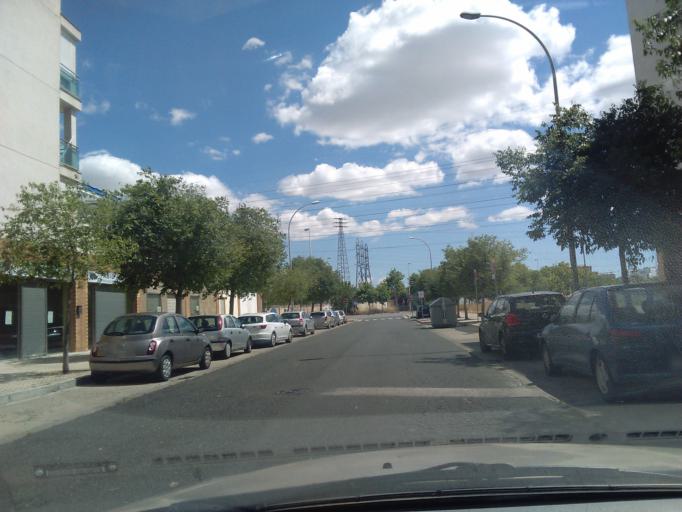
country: ES
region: Andalusia
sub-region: Provincia de Sevilla
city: Sevilla
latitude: 37.4188
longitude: -5.9855
